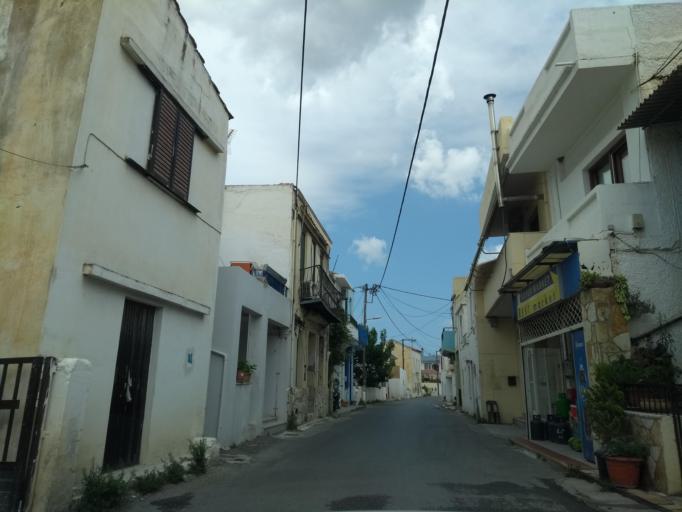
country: GR
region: Crete
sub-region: Nomos Chanias
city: Kalivai
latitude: 35.4545
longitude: 24.1708
